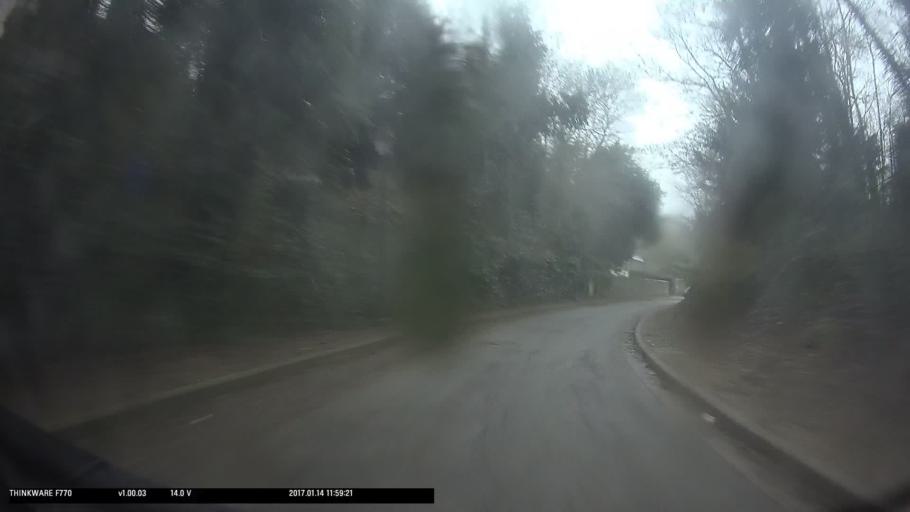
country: FR
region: Ile-de-France
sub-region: Departement du Val-d'Oise
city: Vigny
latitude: 49.0797
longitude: 1.9313
